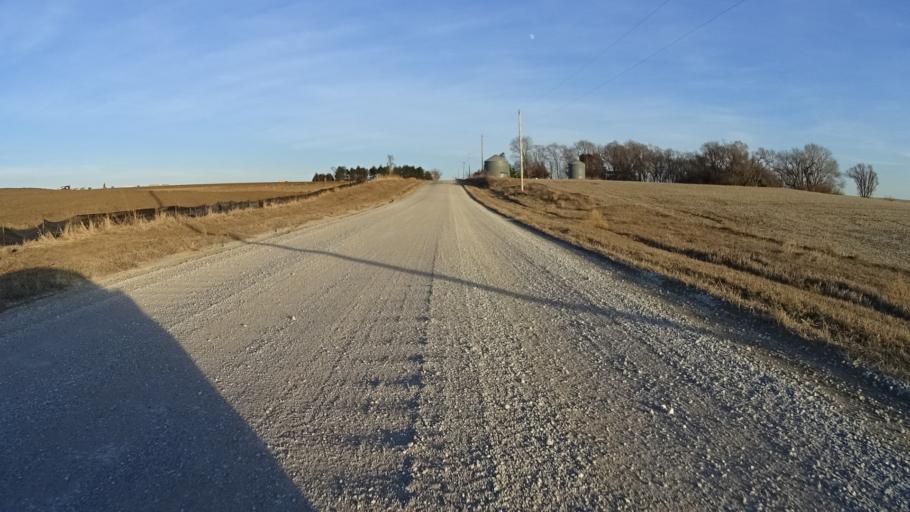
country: US
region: Nebraska
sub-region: Sarpy County
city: Springfield
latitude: 41.1326
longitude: -96.1097
